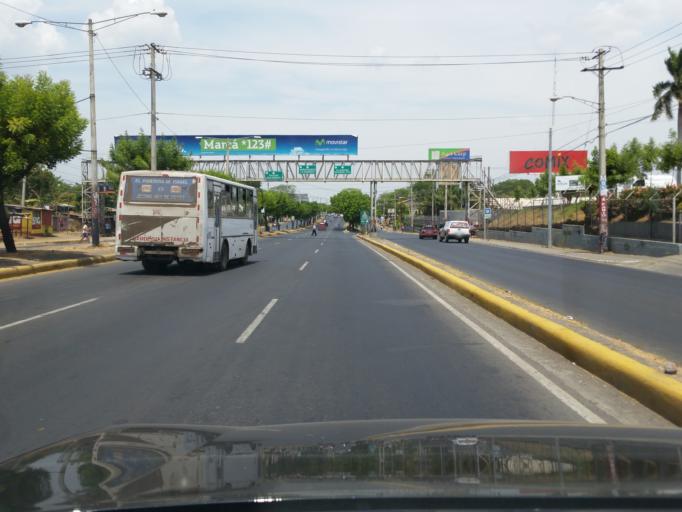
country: NI
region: Managua
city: Managua
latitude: 12.1500
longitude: -86.2184
